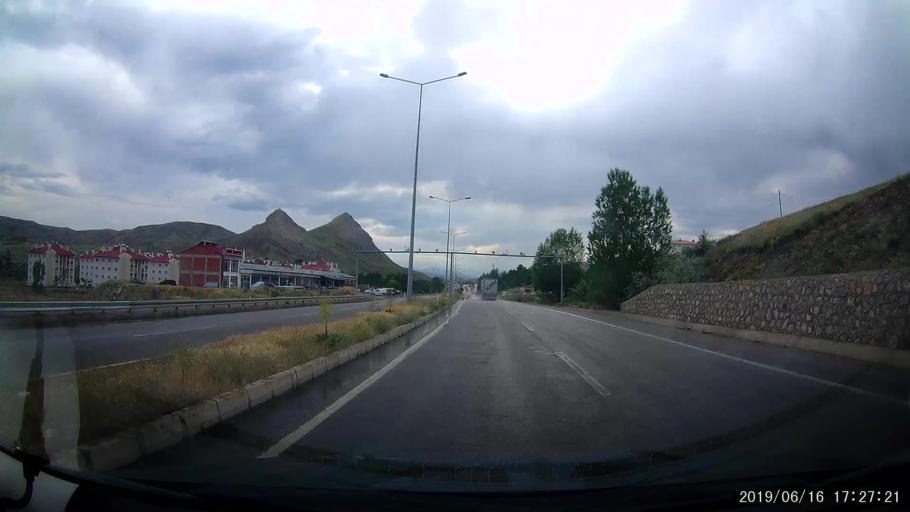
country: TR
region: Erzincan
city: Tercan
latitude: 39.7759
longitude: 40.3948
